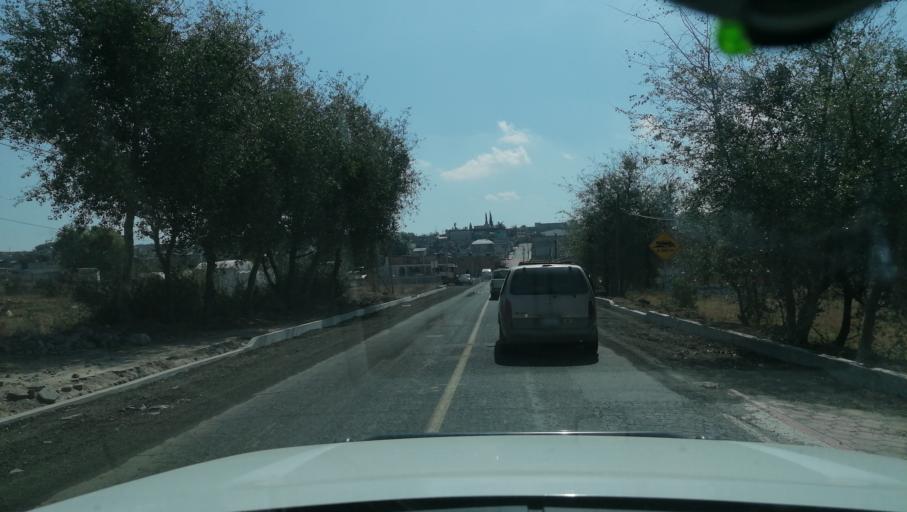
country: MX
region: Tlaxcala
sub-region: San Jeronimo Zacualpan
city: San Jeronimo Zacualpan
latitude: 19.2381
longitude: -98.2561
